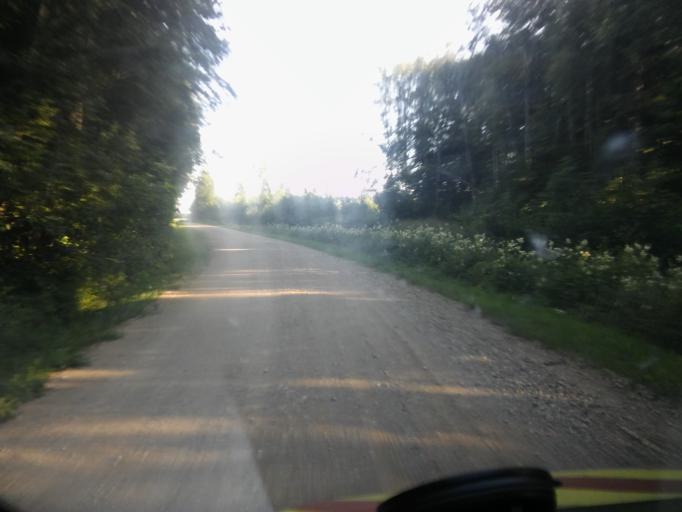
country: EE
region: Valgamaa
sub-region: Torva linn
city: Torva
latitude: 58.0735
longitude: 25.9019
